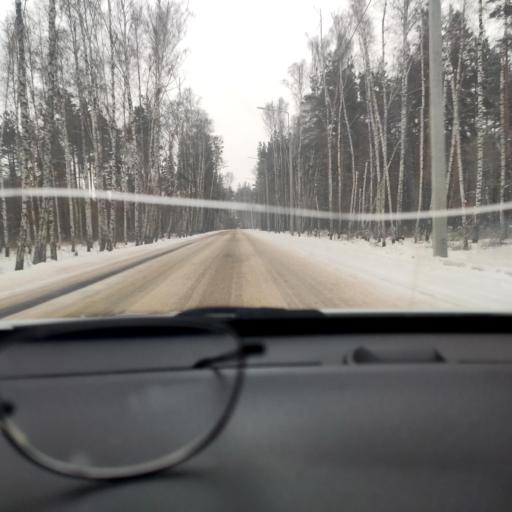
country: RU
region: Voronezj
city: Somovo
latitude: 51.6987
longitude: 39.2818
